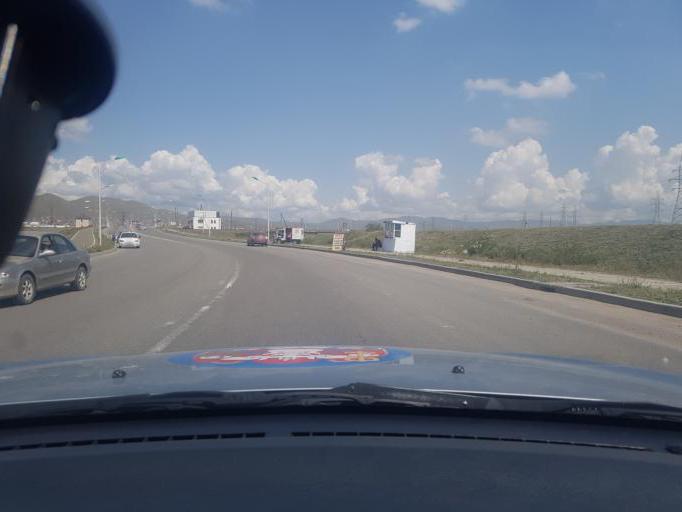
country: MN
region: Ulaanbaatar
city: Ulaanbaatar
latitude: 47.8997
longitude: 107.0270
